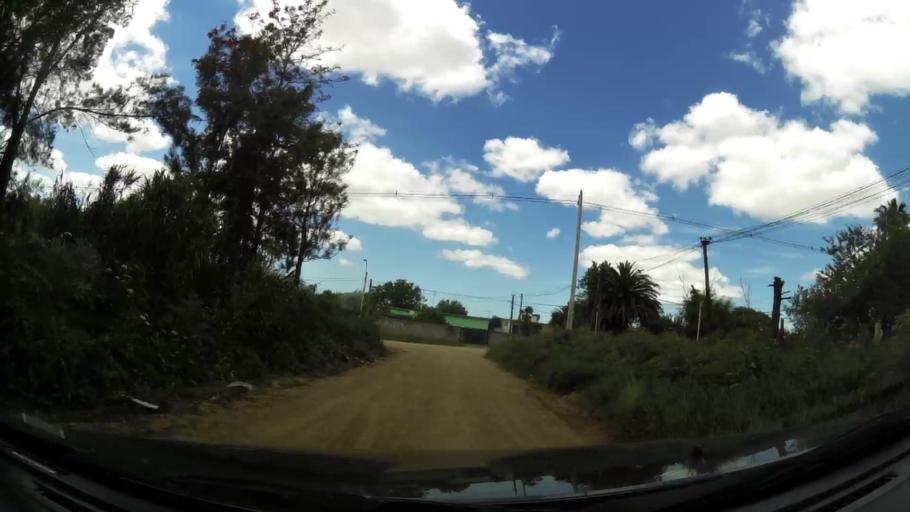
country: UY
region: Canelones
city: Colonia Nicolich
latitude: -34.8191
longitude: -56.0047
